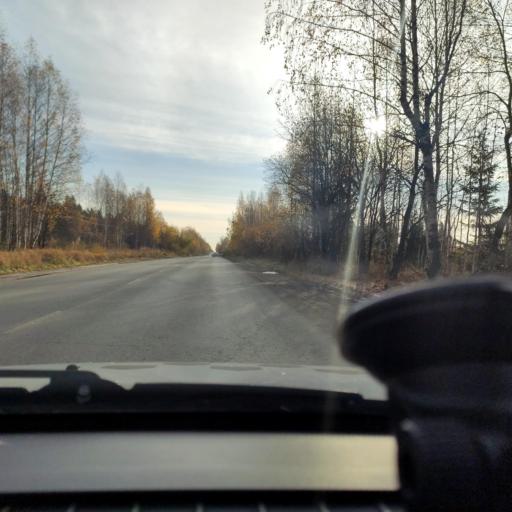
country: RU
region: Perm
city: Ferma
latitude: 57.9453
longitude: 56.4188
